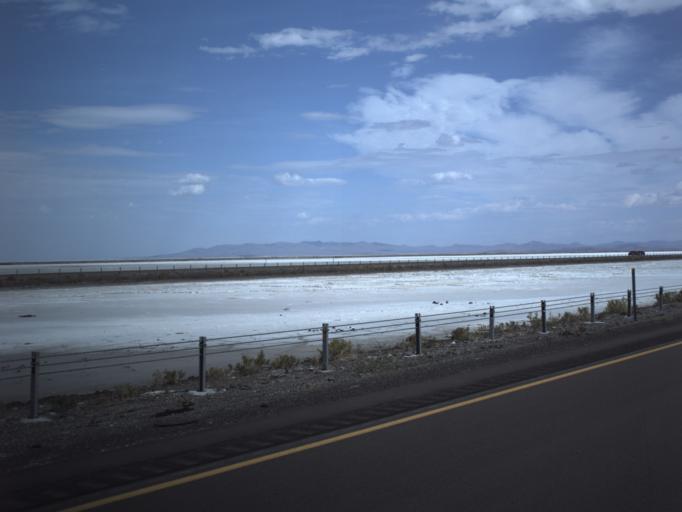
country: US
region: Utah
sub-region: Tooele County
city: Wendover
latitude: 40.7289
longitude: -113.4173
